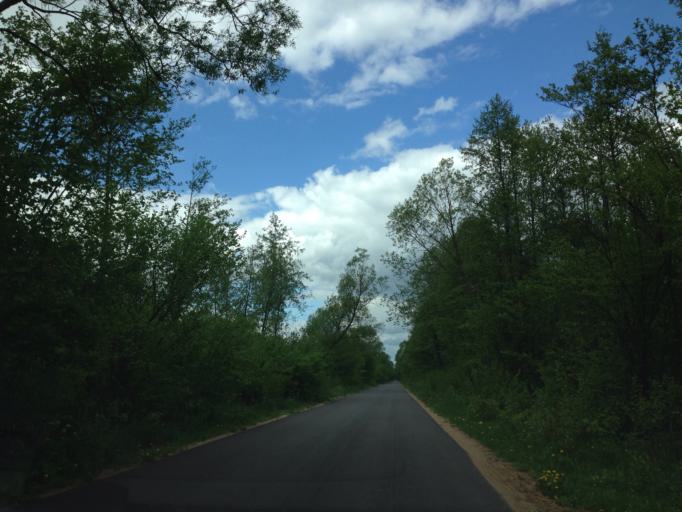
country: PL
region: Podlasie
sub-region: Powiat bialostocki
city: Tykocin
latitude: 53.3216
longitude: 22.6014
